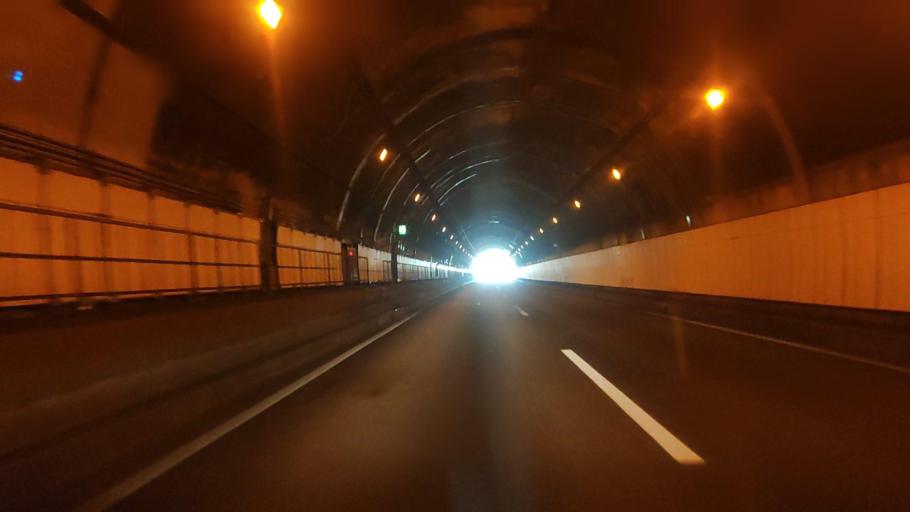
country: JP
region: Miyazaki
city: Miyazaki-shi
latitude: 31.8227
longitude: 131.2472
